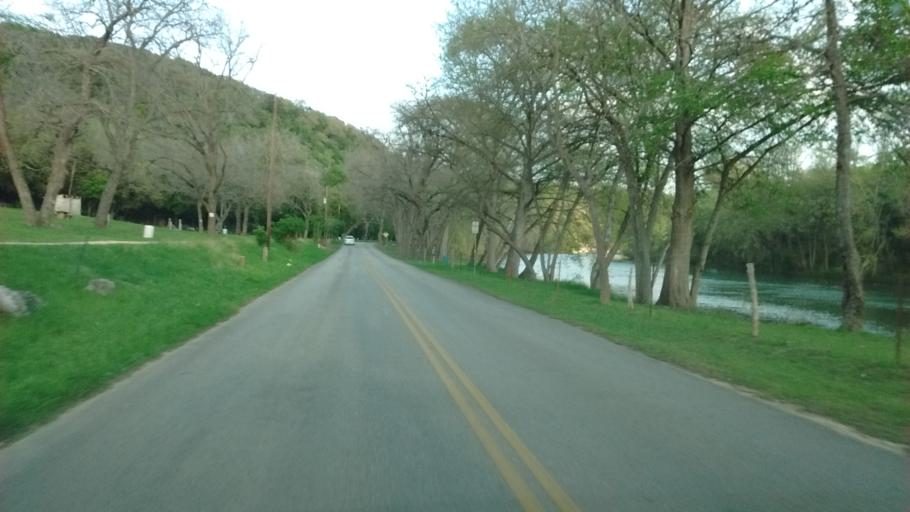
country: US
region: Texas
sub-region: Comal County
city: New Braunfels
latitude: 29.7668
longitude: -98.1471
